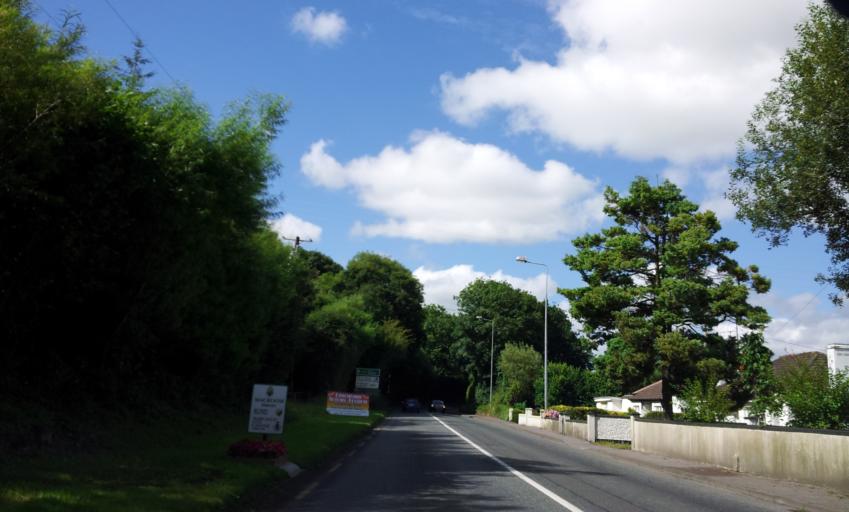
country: IE
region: Munster
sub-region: County Cork
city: Macroom
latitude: 51.8987
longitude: -8.9405
